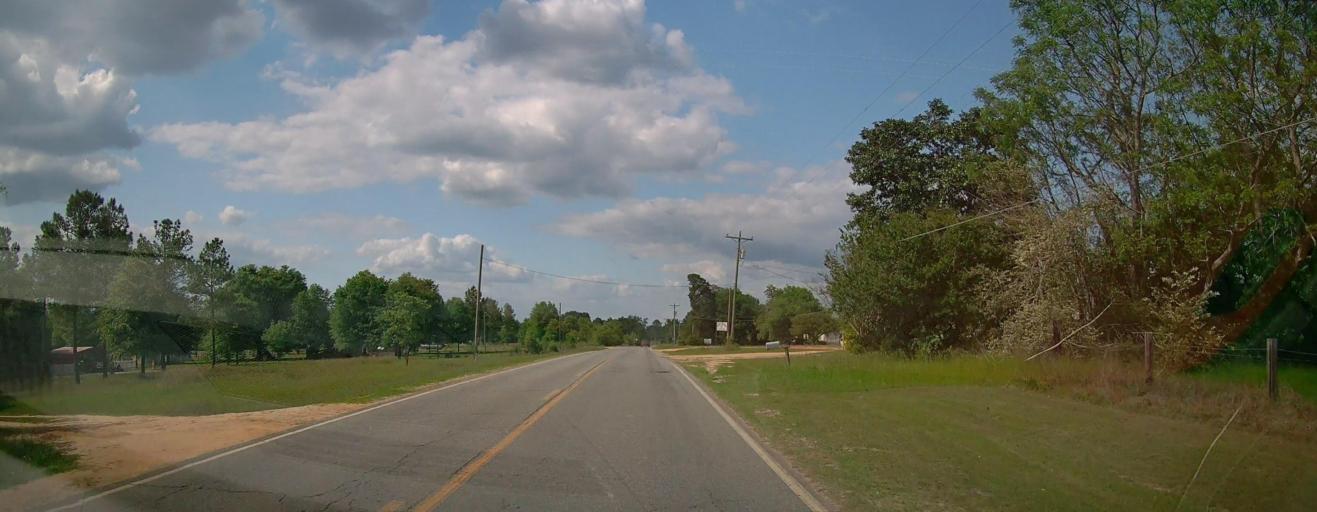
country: US
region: Georgia
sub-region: Laurens County
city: East Dublin
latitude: 32.5901
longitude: -82.8651
